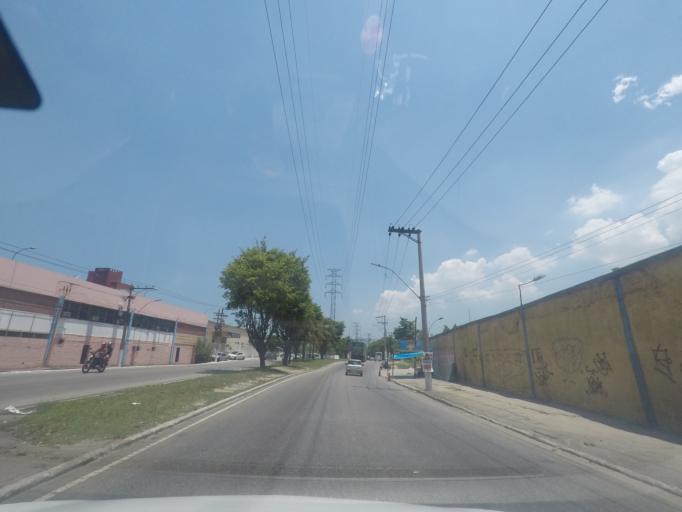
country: BR
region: Rio de Janeiro
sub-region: Duque De Caxias
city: Duque de Caxias
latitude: -22.7952
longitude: -43.3055
